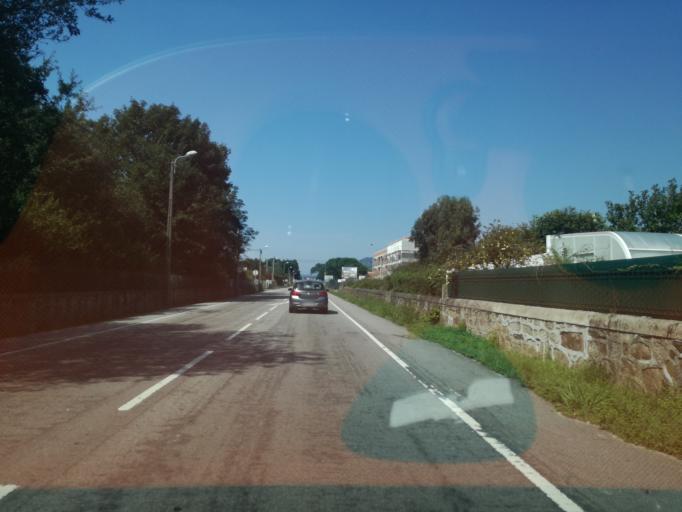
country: PT
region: Braga
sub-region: Esposende
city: Esposende
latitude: 41.5416
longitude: -8.7820
